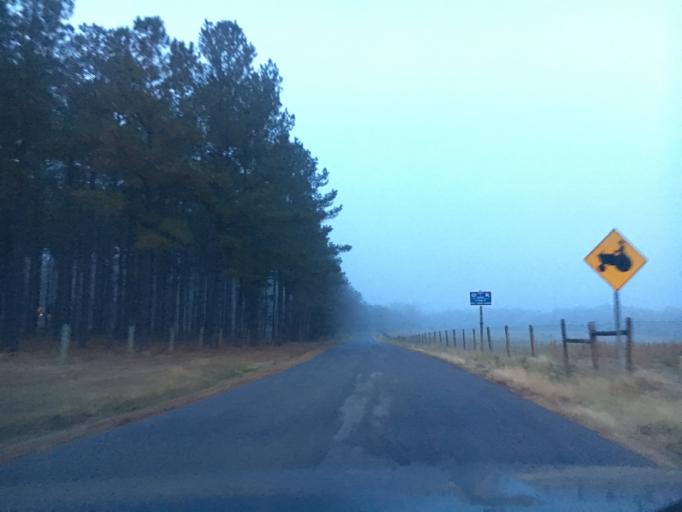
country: US
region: Virginia
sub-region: Halifax County
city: Mountain Road
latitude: 36.6835
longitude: -79.0324
